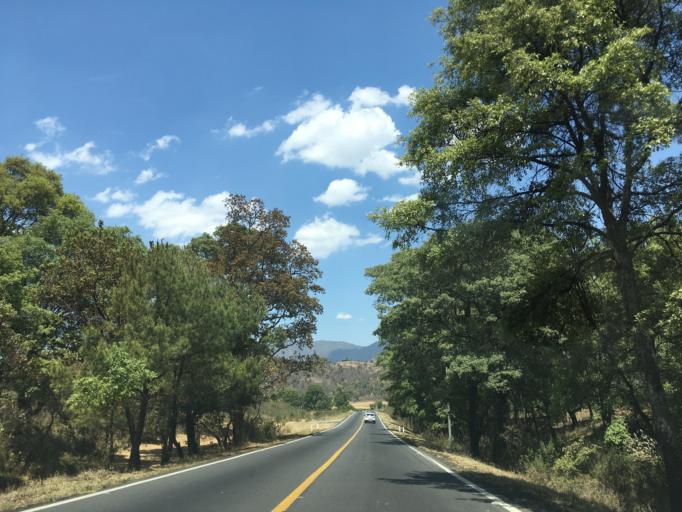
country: MX
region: Michoacan
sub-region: Chilchota
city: Tacuro (Santa Maria Tacuro)
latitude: 19.8317
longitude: -102.0310
